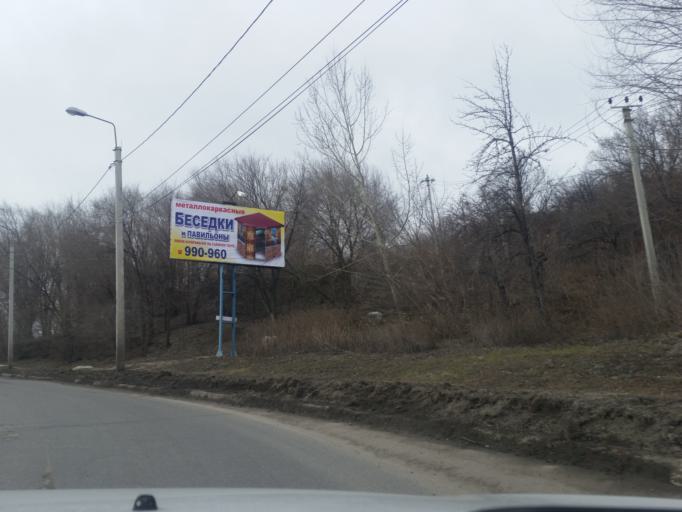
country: RU
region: Ulyanovsk
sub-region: Ulyanovskiy Rayon
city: Ulyanovsk
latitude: 54.3100
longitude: 48.4060
